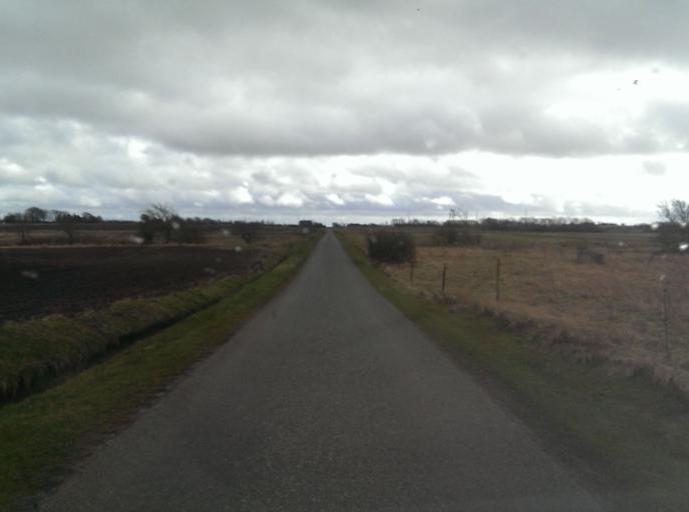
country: DK
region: South Denmark
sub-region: Esbjerg Kommune
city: Bramming
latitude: 55.4420
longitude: 8.6777
